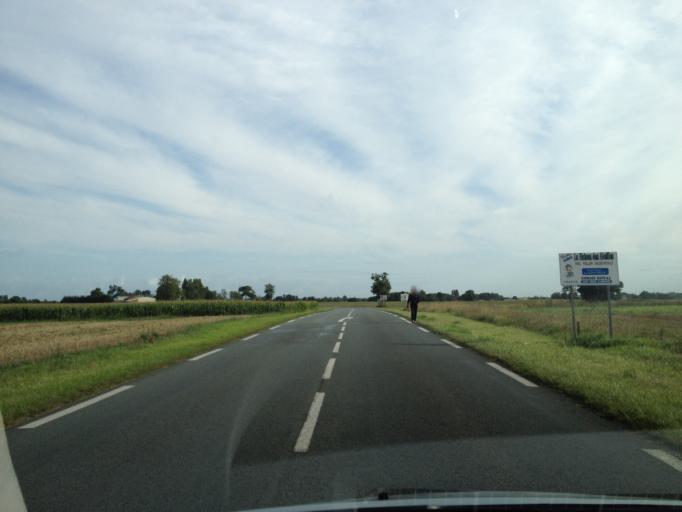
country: FR
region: Poitou-Charentes
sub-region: Departement de la Charente-Maritime
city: Le Gua
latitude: 45.7417
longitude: -0.9494
